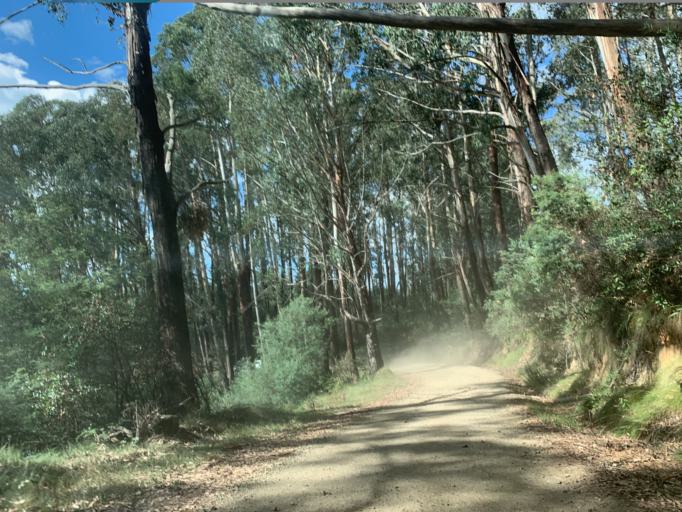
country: AU
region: Victoria
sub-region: Mansfield
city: Mansfield
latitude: -37.0933
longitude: 146.5411
